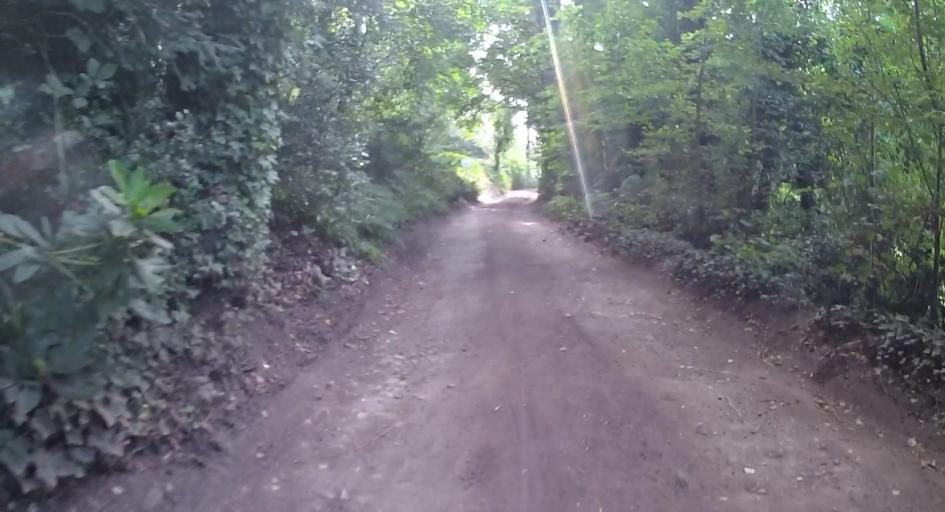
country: GB
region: England
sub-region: Surrey
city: Farnham
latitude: 51.1946
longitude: -0.8038
